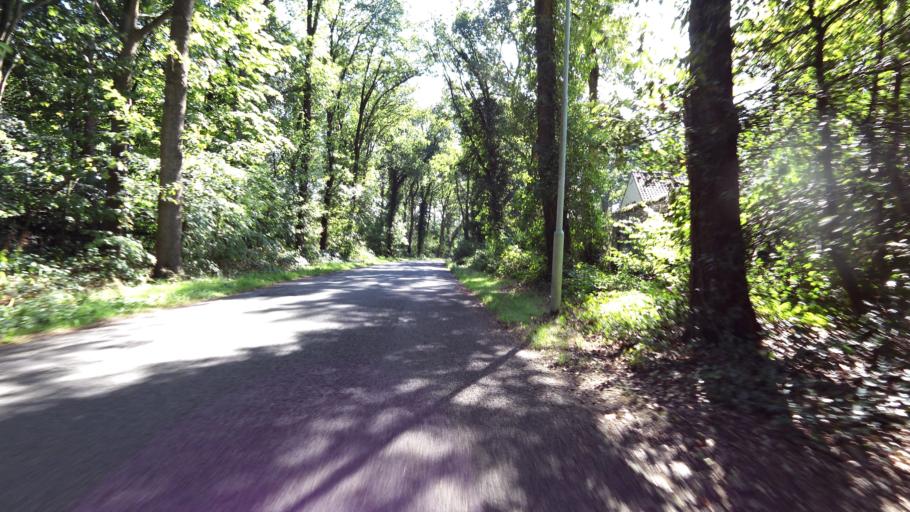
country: NL
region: Gelderland
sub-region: Gemeente Renkum
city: Heelsum
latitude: 51.9845
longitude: 5.7611
